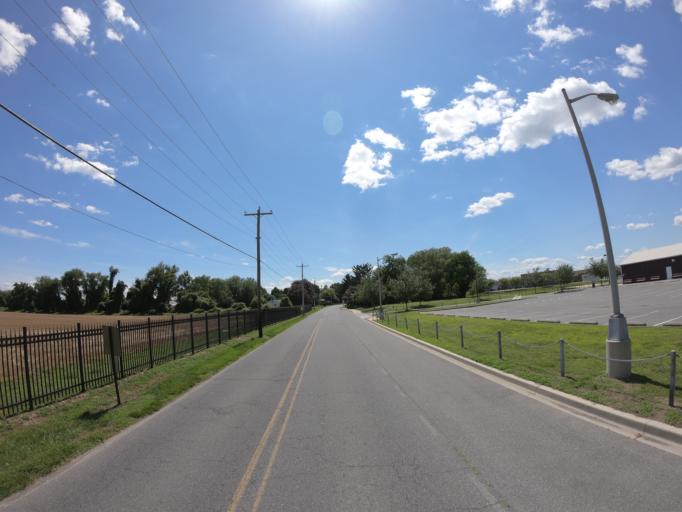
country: US
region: Delaware
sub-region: Sussex County
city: Milford
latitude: 38.9287
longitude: -75.4237
